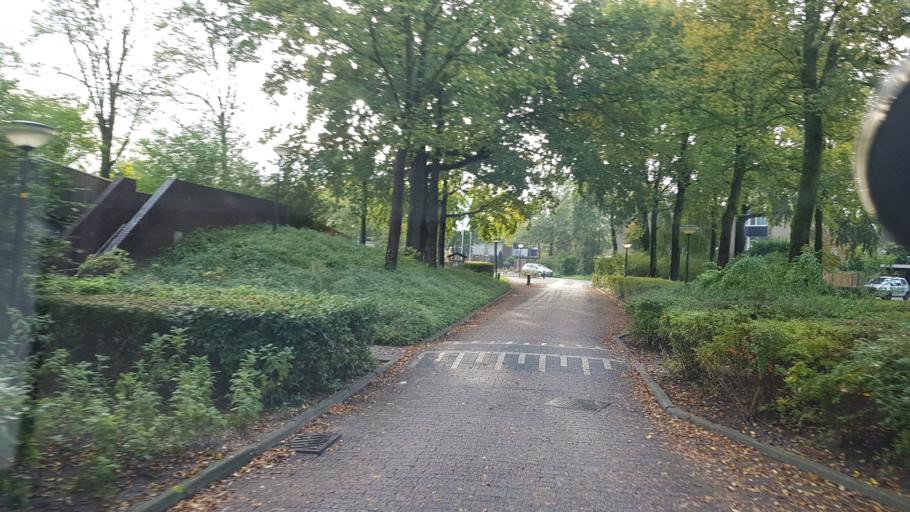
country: NL
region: Gelderland
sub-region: Gemeente Apeldoorn
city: Apeldoorn
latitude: 52.2032
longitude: 5.9846
